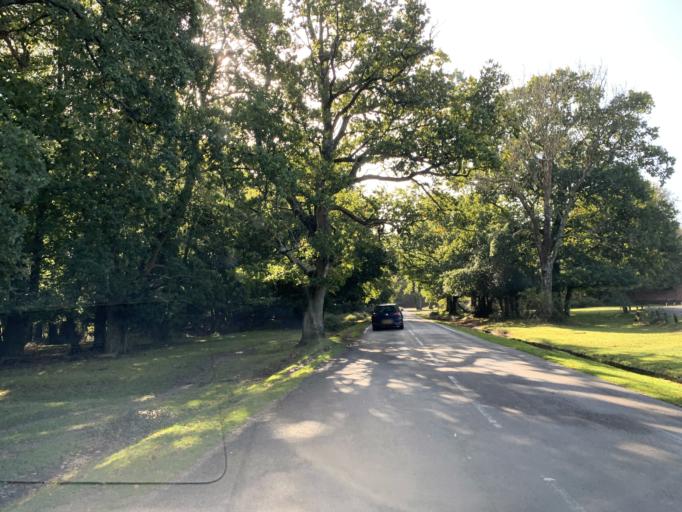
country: GB
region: England
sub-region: Hampshire
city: Cadnam
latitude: 50.9283
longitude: -1.6553
